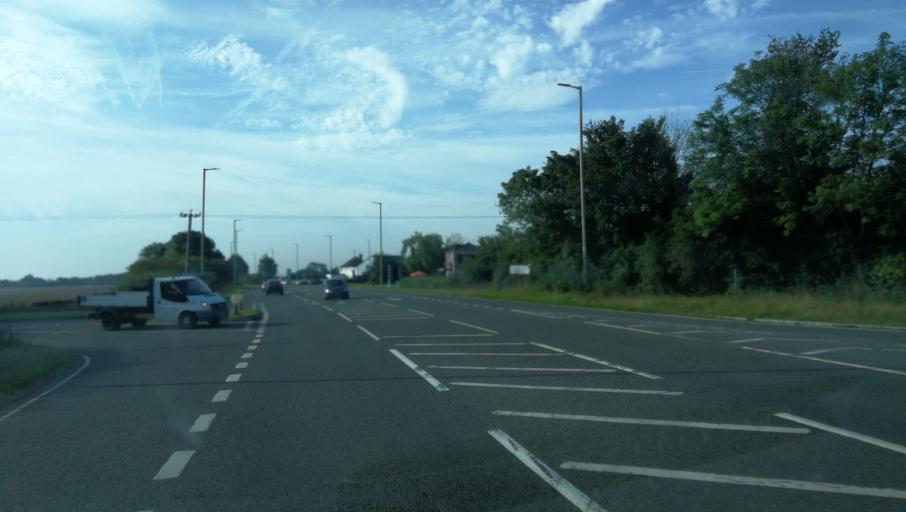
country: GB
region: England
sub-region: Oxfordshire
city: Woodstock
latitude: 51.8714
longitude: -1.3291
